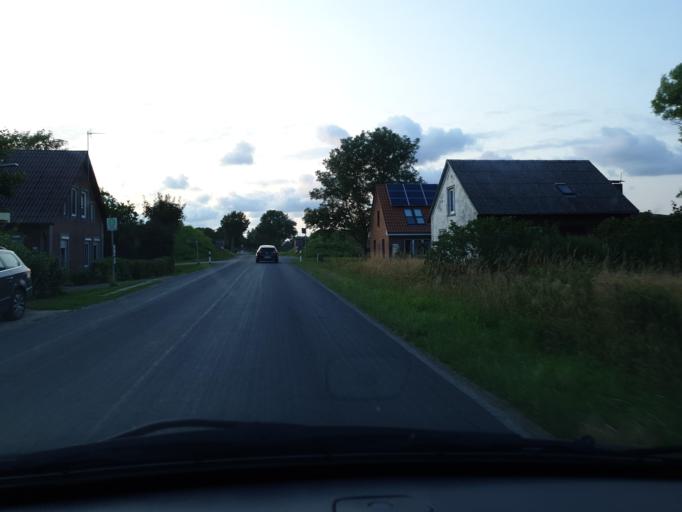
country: DE
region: Schleswig-Holstein
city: Kronprinzenkoog
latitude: 53.9541
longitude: 8.9364
